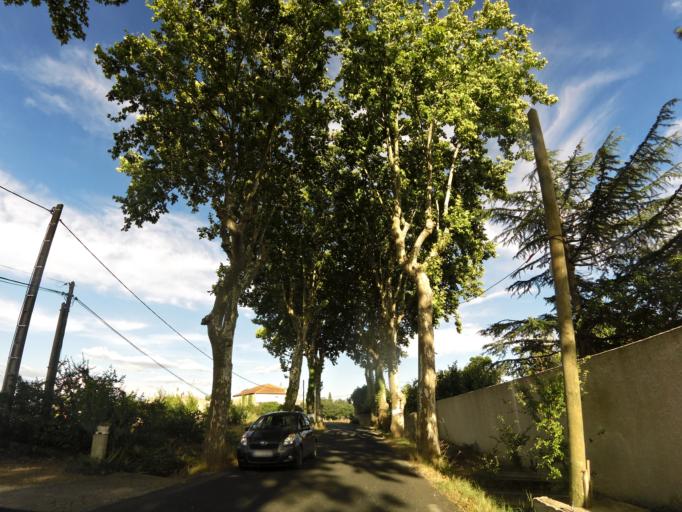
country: FR
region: Languedoc-Roussillon
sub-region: Departement de l'Herault
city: Beaulieu
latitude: 43.7699
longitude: 4.0168
